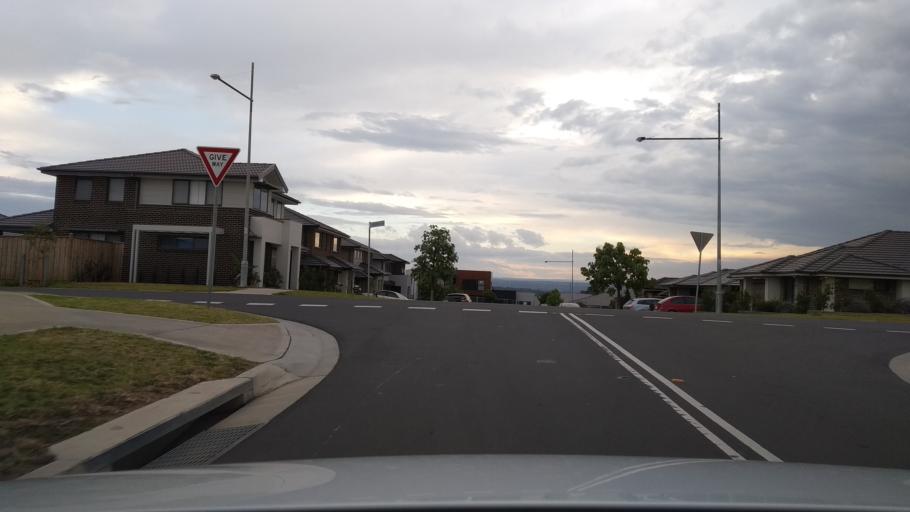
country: AU
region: New South Wales
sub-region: Camden
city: Narellan
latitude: -34.0031
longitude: 150.7287
